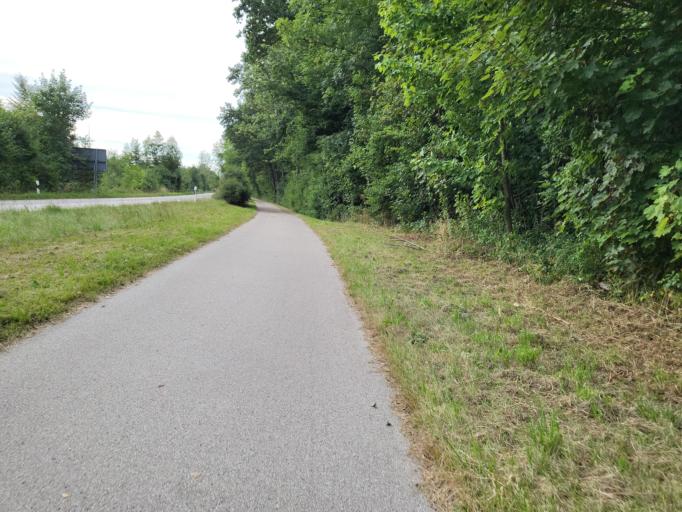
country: DE
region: Bavaria
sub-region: Upper Bavaria
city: Hohenkirchen-Siegertsbrunn
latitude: 48.0105
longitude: 11.7209
